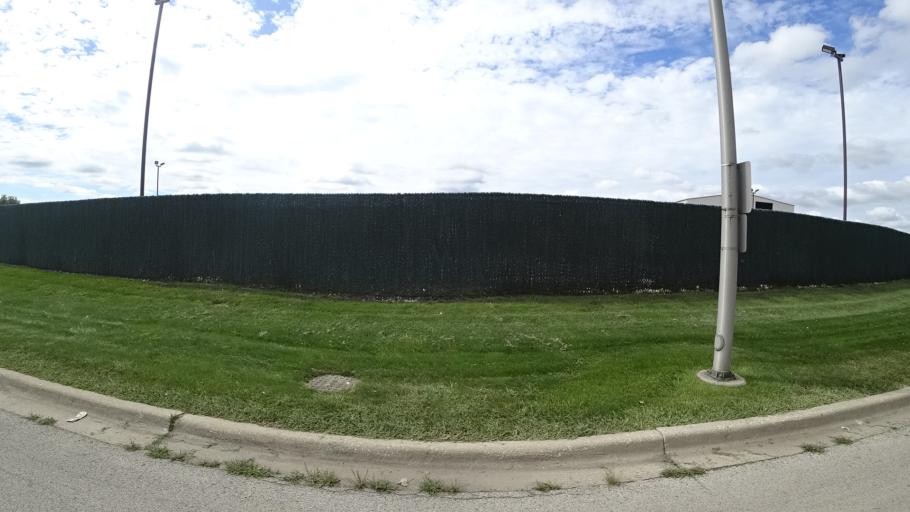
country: US
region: Illinois
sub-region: Cook County
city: Chicago Ridge
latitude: 41.7093
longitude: -87.7861
